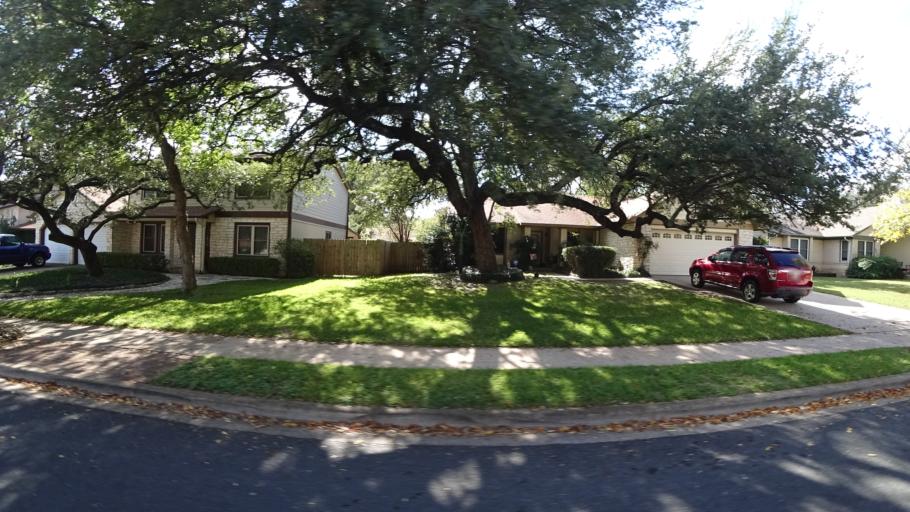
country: US
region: Texas
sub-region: Travis County
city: Wells Branch
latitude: 30.4198
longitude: -97.7228
